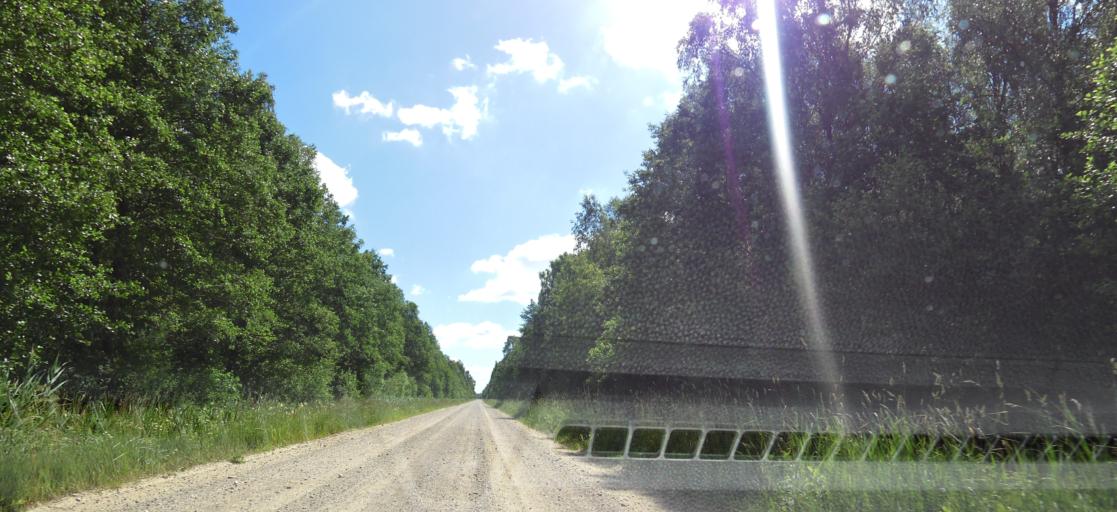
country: LT
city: Vabalninkas
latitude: 56.0030
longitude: 24.8581
